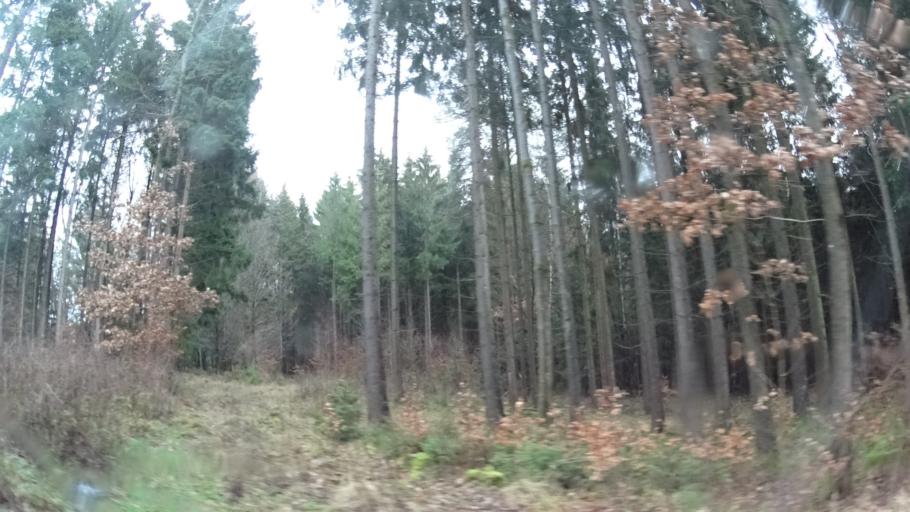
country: DE
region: Bavaria
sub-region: Regierungsbezirk Unterfranken
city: Willmars
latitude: 50.5305
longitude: 10.2280
